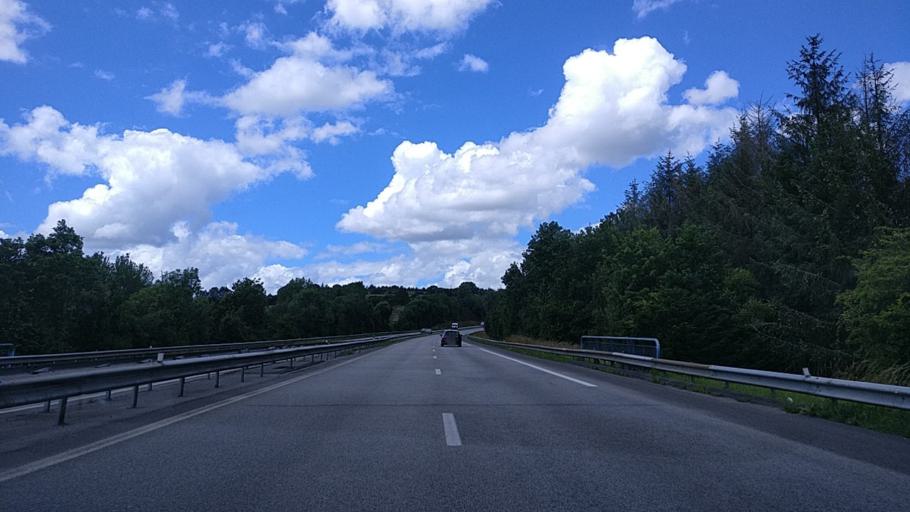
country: FR
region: Brittany
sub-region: Departement du Finistere
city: Dineault
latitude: 48.2660
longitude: -4.1153
